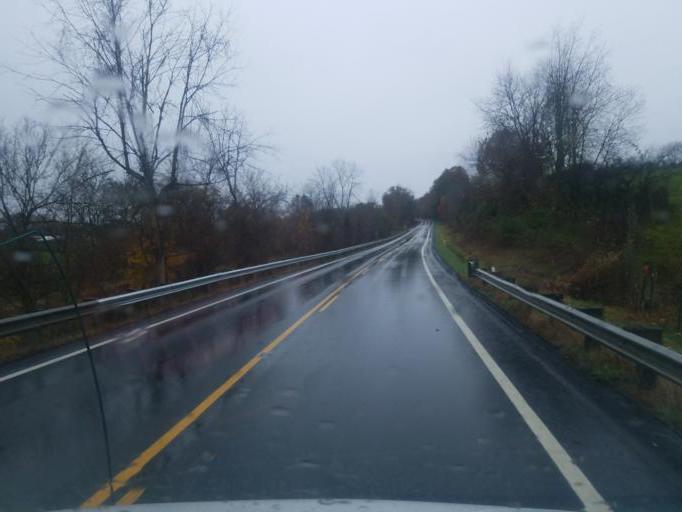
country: US
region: Ohio
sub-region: Washington County
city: Beverly
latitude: 39.4609
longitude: -81.6374
